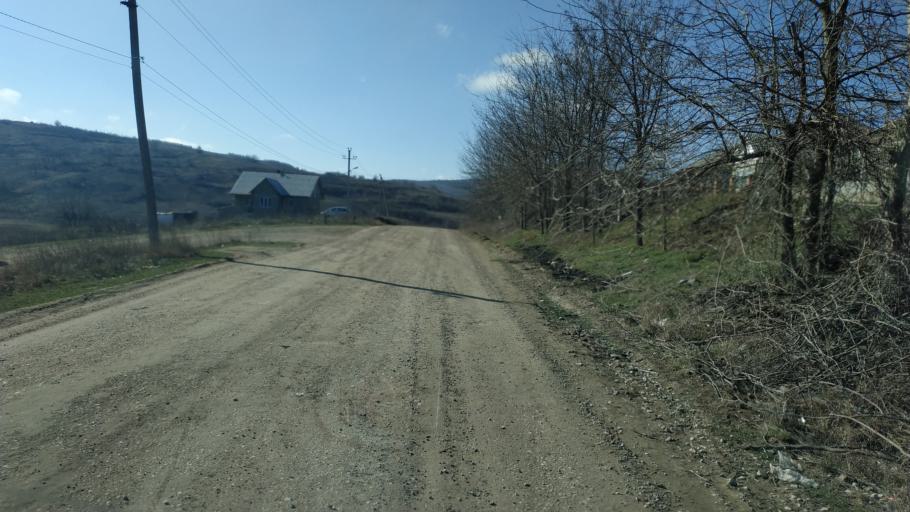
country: MD
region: Hincesti
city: Hincesti
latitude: 46.9309
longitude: 28.6347
